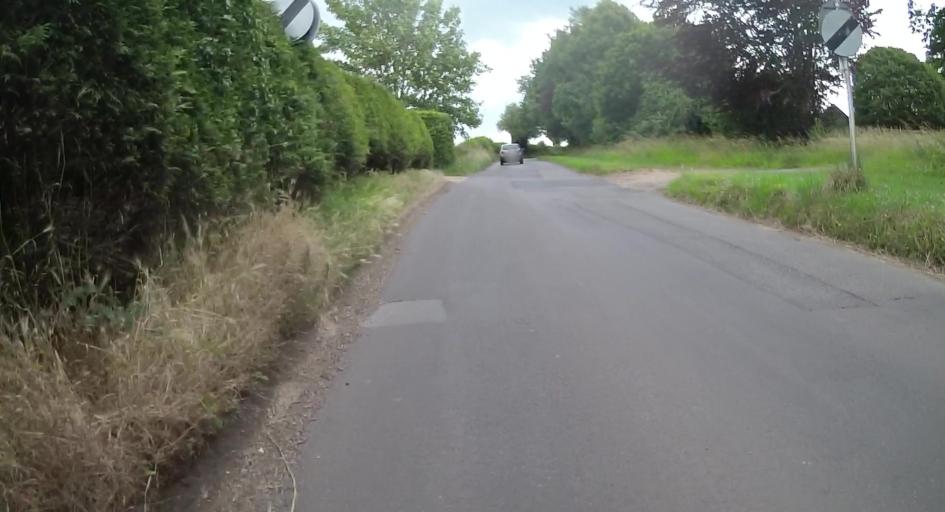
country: GB
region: England
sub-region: Surrey
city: Farnham
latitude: 51.2283
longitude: -0.8556
